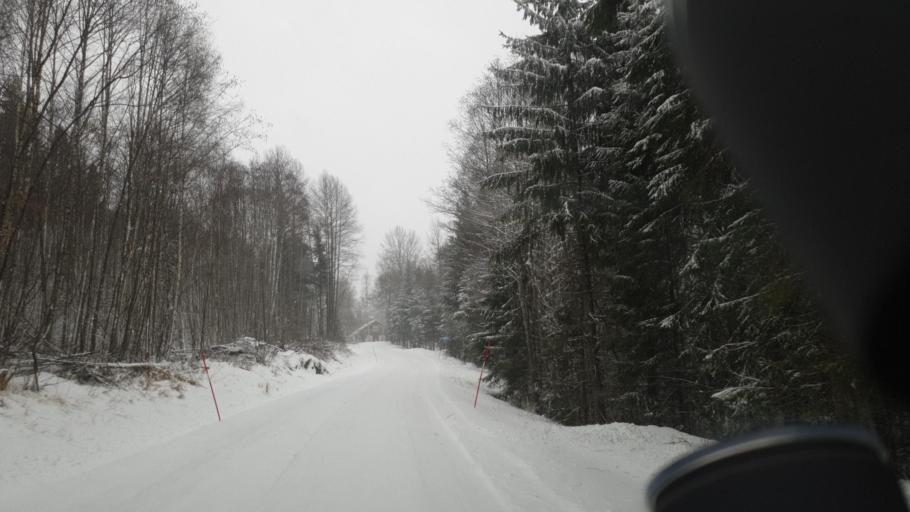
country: SE
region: Vaermland
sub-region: Sunne Kommun
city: Sunne
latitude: 59.6970
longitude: 12.8846
